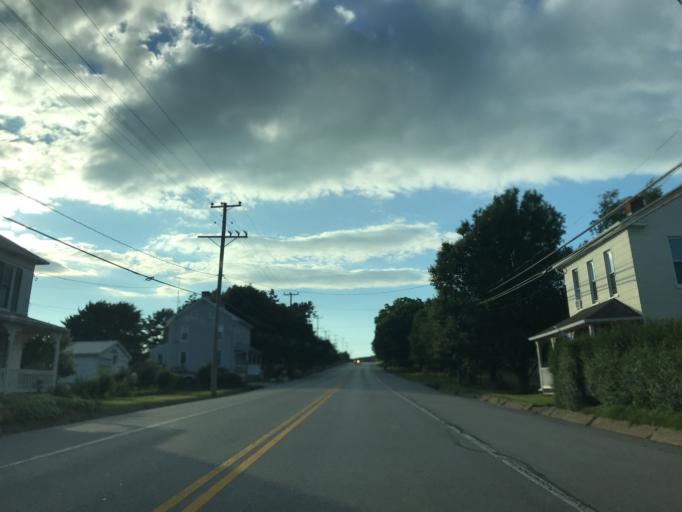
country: US
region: Maryland
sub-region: Carroll County
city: Manchester
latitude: 39.6916
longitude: -76.8993
